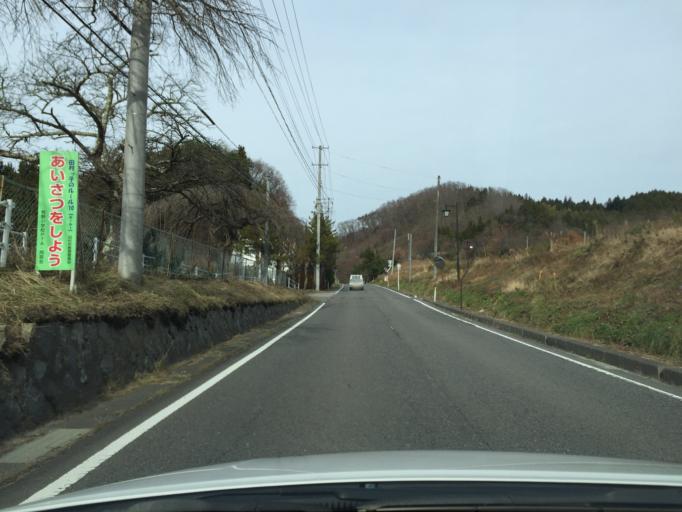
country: JP
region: Fukushima
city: Funehikimachi-funehiki
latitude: 37.3714
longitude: 140.6006
